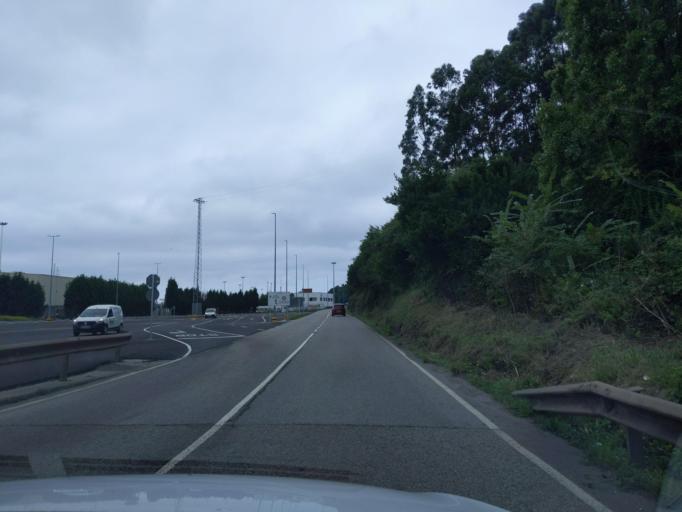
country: ES
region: Asturias
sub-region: Province of Asturias
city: Aviles
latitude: 43.5651
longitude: -5.9159
